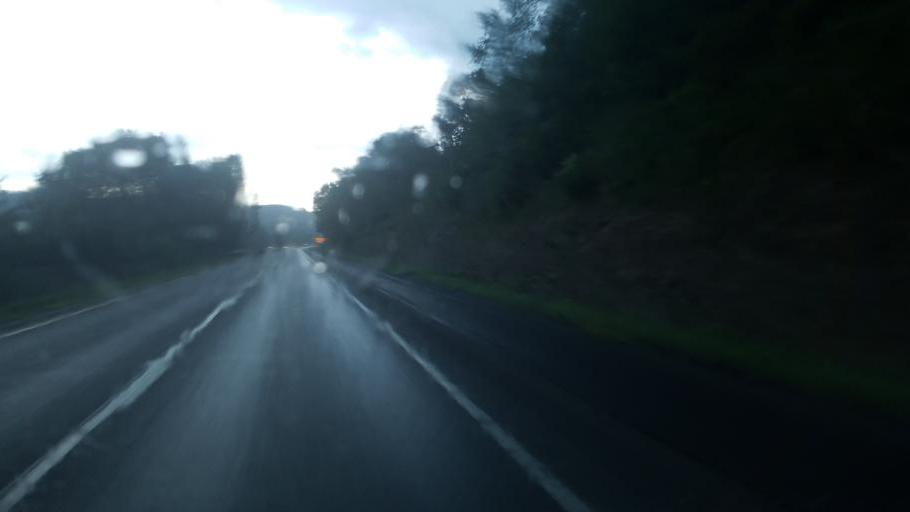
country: US
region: Pennsylvania
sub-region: Butler County
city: Prospect
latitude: 40.8846
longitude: -80.1172
